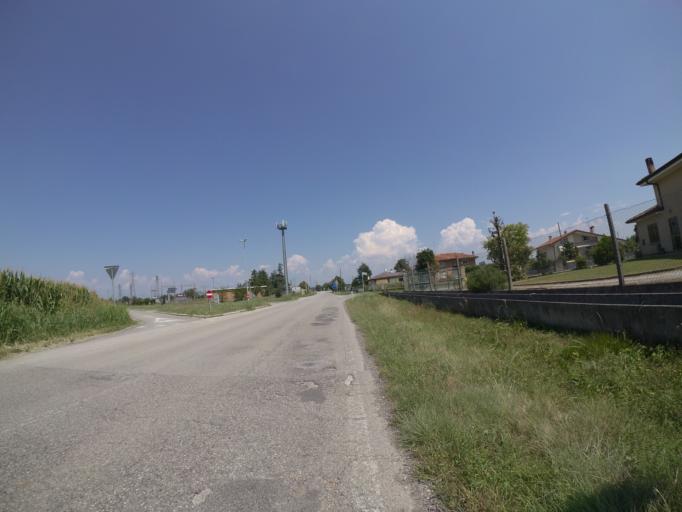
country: IT
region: Friuli Venezia Giulia
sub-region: Provincia di Udine
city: Mortegliano
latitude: 45.9278
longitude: 13.1529
